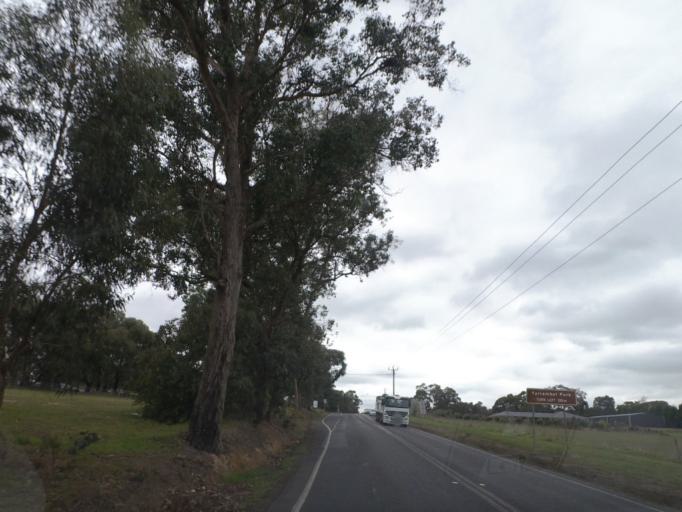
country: AU
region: Victoria
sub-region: Nillumbik
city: Doreen
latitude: -37.6276
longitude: 145.1343
